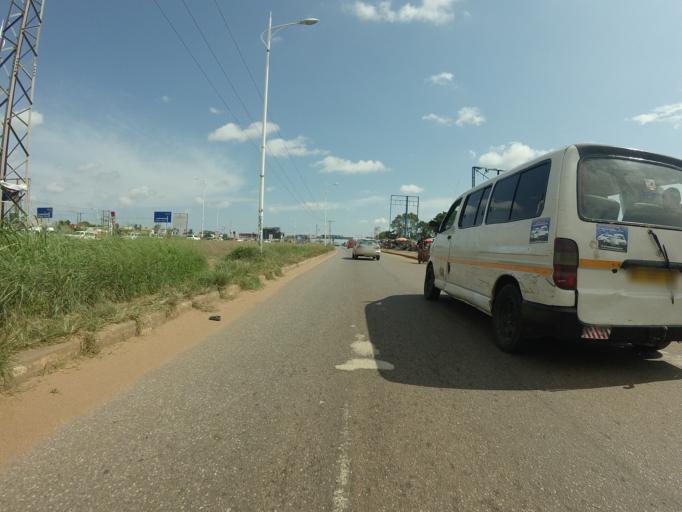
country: GH
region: Greater Accra
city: Medina Estates
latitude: 5.7074
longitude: -0.1715
